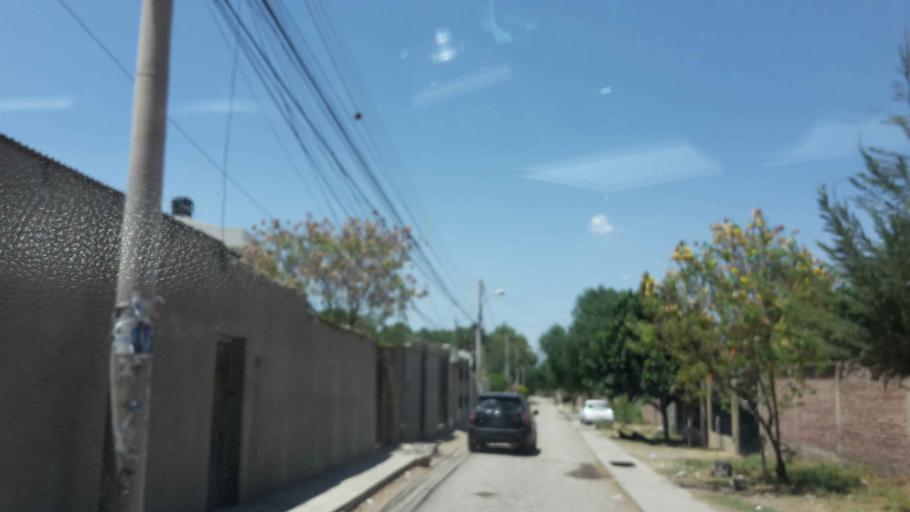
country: BO
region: Cochabamba
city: Cochabamba
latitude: -17.3677
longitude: -66.1948
